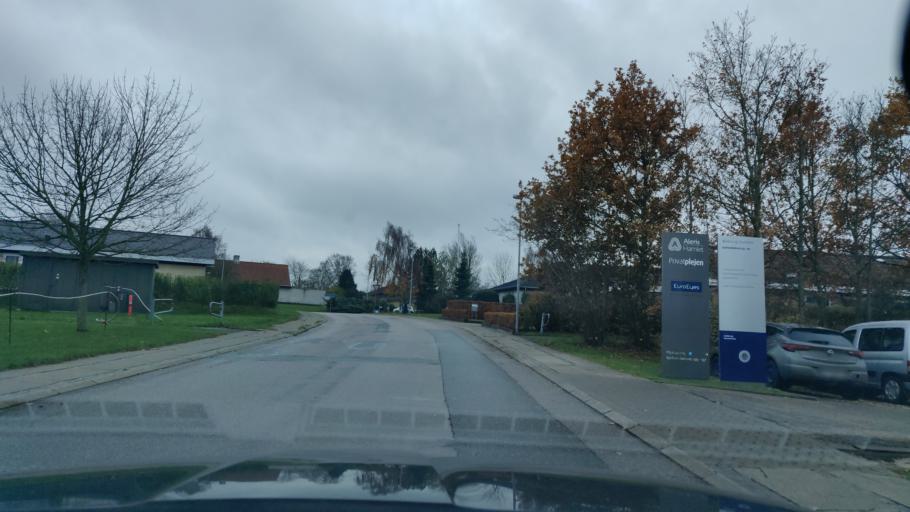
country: DK
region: North Denmark
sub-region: Alborg Kommune
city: Aalborg
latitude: 57.0173
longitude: 9.8784
